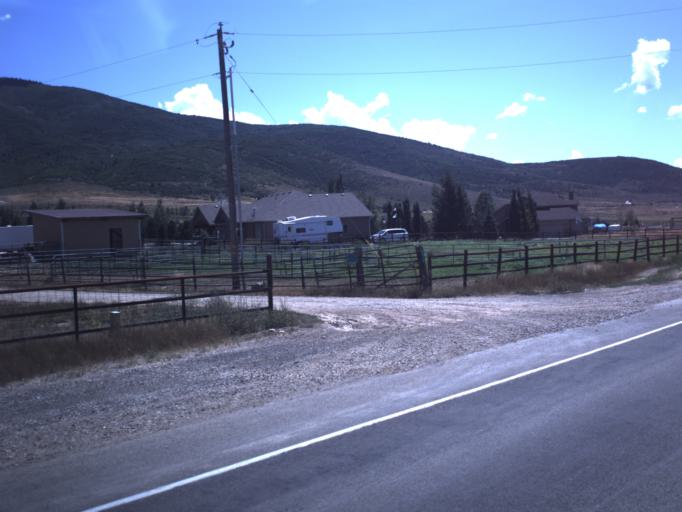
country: US
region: Utah
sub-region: Summit County
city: Kamas
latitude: 40.6741
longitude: -111.2809
